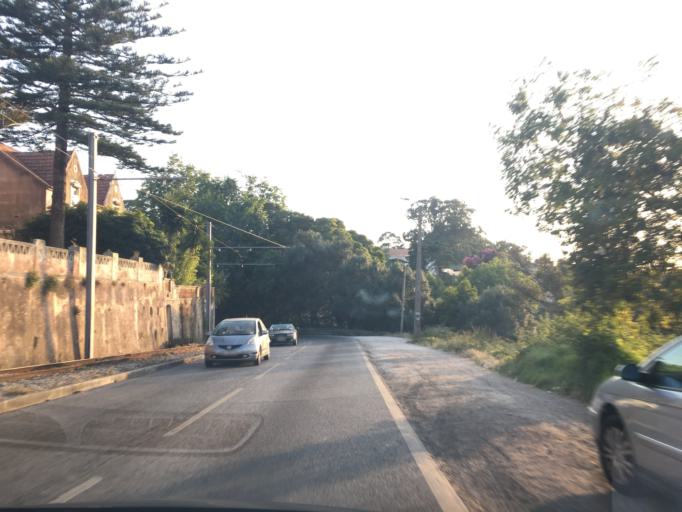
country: PT
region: Lisbon
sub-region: Sintra
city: Sintra
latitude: 38.8045
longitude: -9.3828
